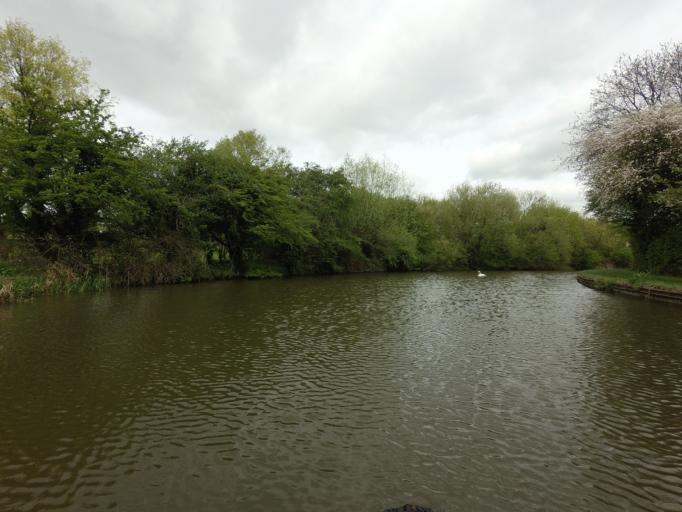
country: GB
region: England
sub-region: Milton Keynes
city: Simpson
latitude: 52.0159
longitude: -0.7202
